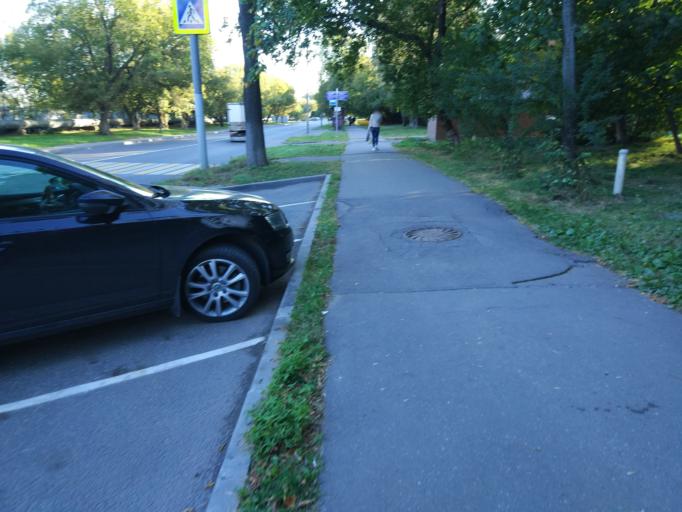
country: RU
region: Moscow
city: Mar'ino
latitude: 55.6709
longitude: 37.7236
